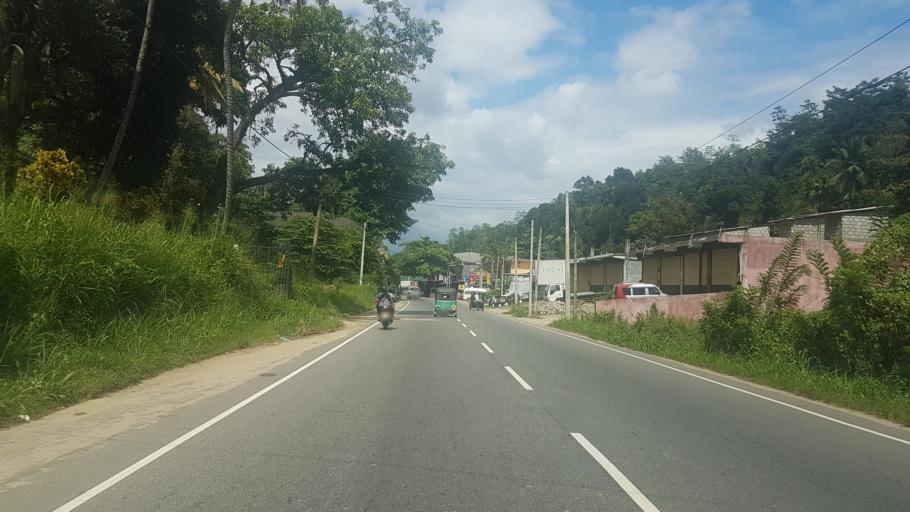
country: LK
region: Central
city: Gampola
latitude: 7.2058
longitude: 80.5991
